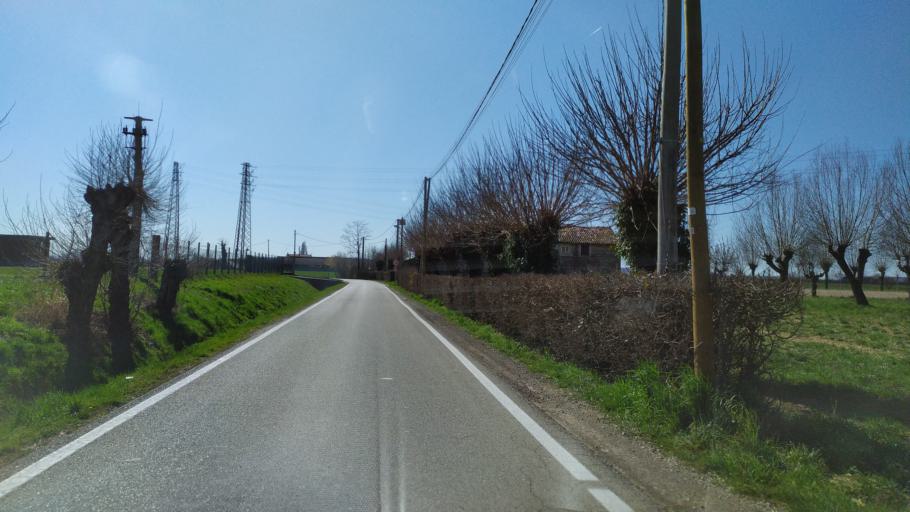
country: IT
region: Veneto
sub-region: Provincia di Vicenza
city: Vigardolo
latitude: 45.6238
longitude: 11.5988
